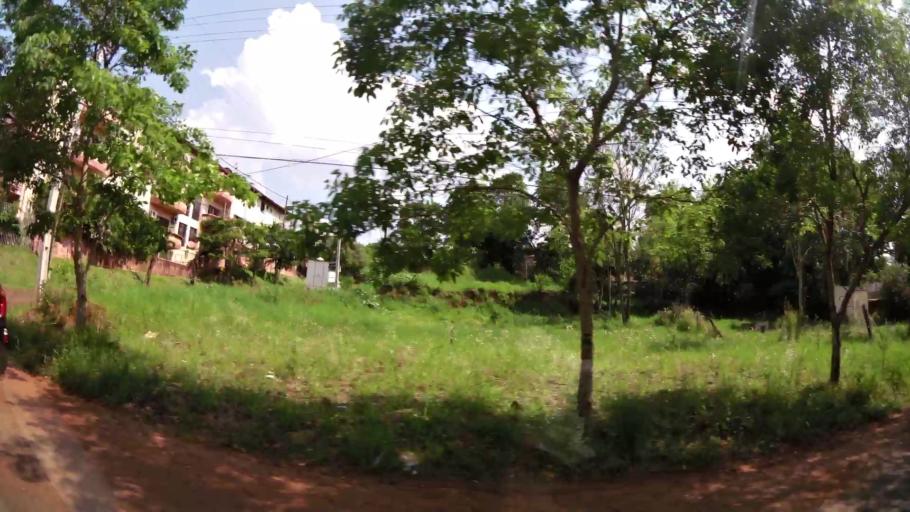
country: PY
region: Alto Parana
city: Ciudad del Este
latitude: -25.5161
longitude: -54.6291
